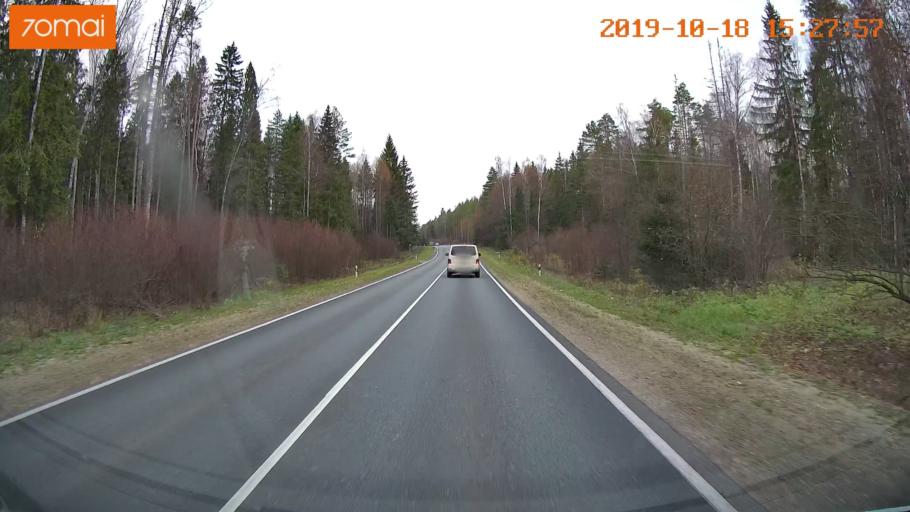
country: RU
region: Vladimir
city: Anopino
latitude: 55.7602
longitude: 40.6729
